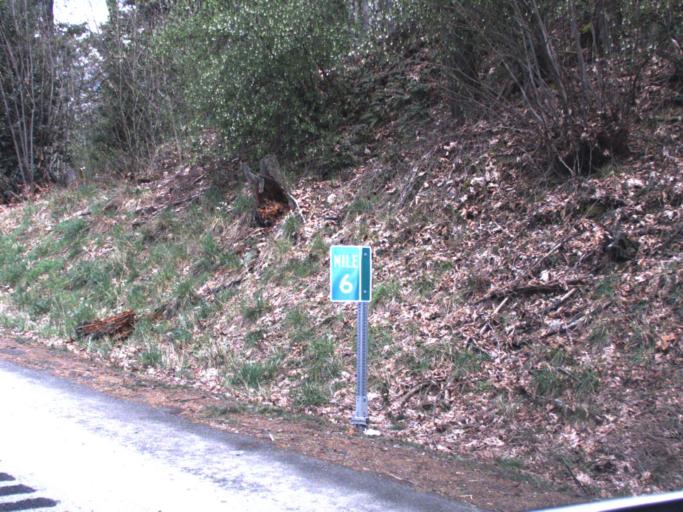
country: US
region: Washington
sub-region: King County
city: Black Diamond
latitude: 47.2875
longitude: -121.9902
